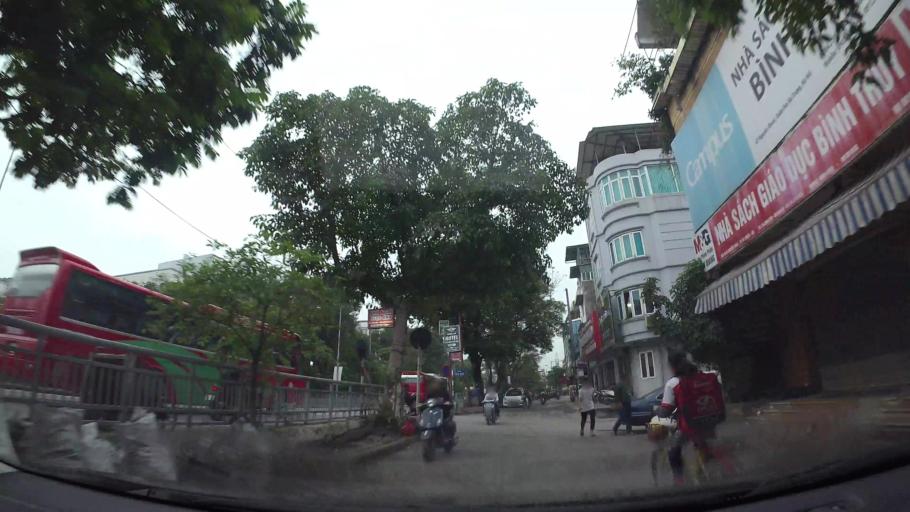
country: VN
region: Ha Noi
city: Hai BaTrung
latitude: 21.0147
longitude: 105.8632
